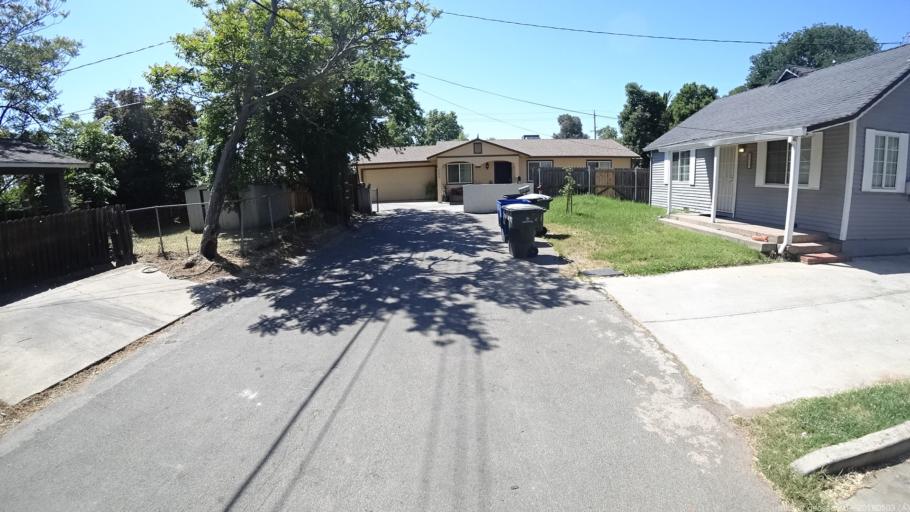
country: US
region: California
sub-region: Sacramento County
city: Sacramento
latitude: 38.6138
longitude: -121.4405
